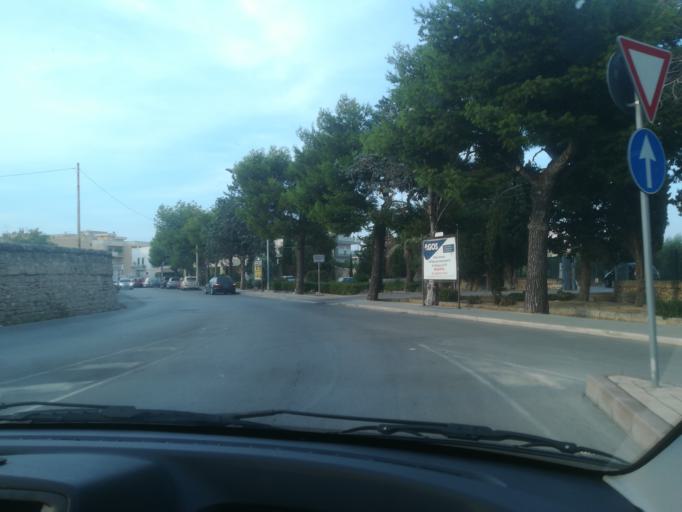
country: IT
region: Apulia
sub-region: Provincia di Bari
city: Monopoli
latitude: 40.9444
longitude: 17.2996
